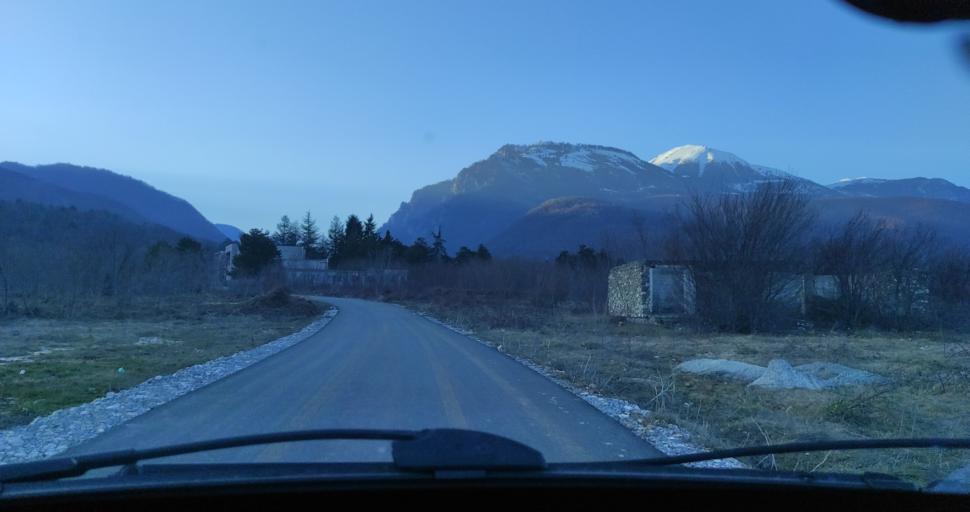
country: XK
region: Gjakova
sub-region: Komuna e Decanit
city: Decan
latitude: 42.5402
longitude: 20.2762
